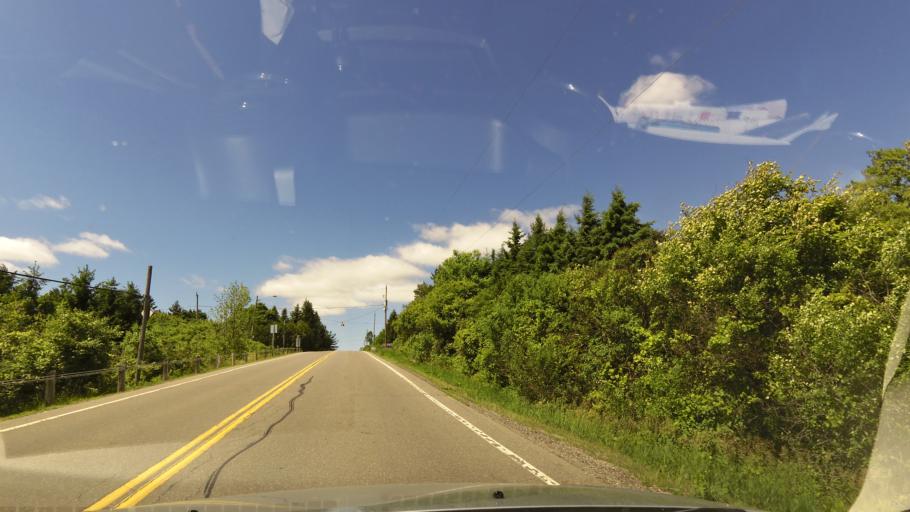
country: CA
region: Ontario
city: Newmarket
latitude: 43.9823
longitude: -79.5429
